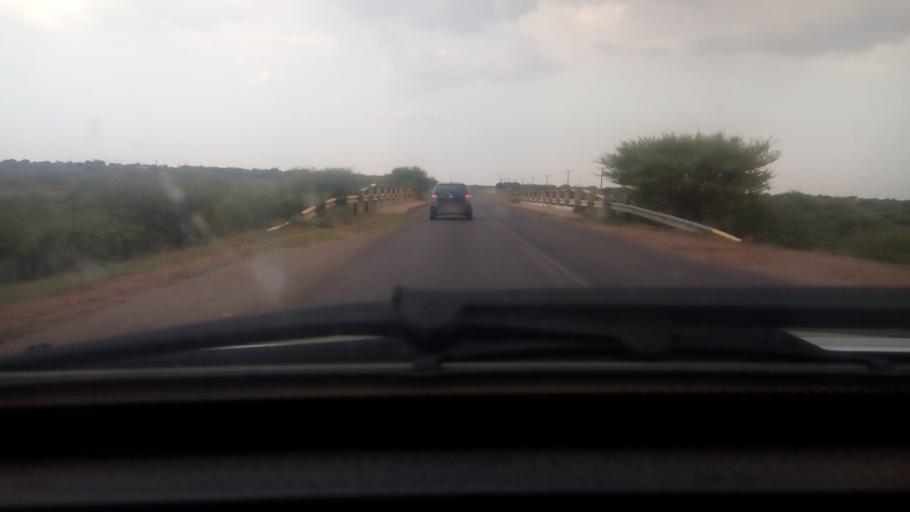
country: BW
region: Kweneng
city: Metsemotlhaba
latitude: -24.4647
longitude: 25.6641
